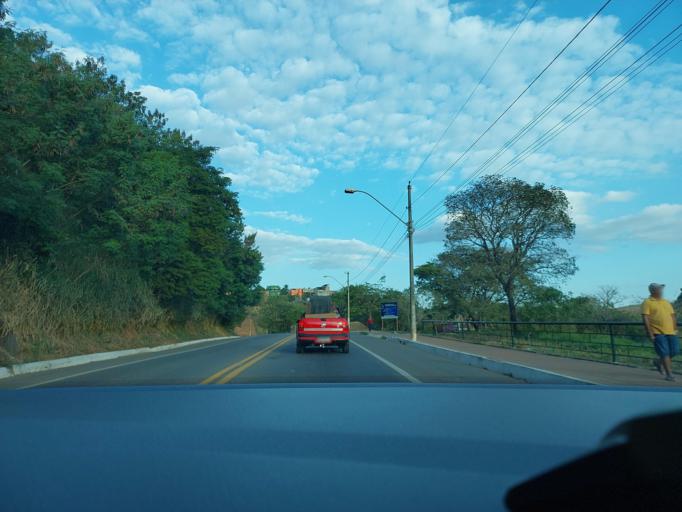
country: BR
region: Minas Gerais
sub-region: Muriae
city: Muriae
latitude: -21.1279
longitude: -42.3501
